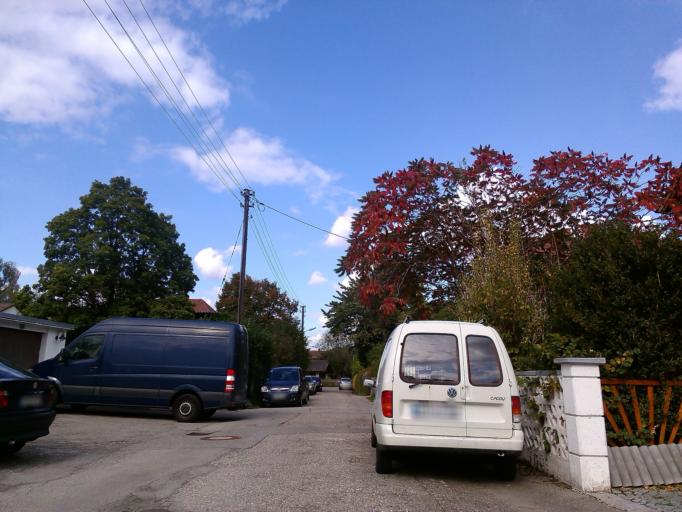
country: DE
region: Bavaria
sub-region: Upper Bavaria
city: Gauting
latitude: 48.0702
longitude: 11.3731
